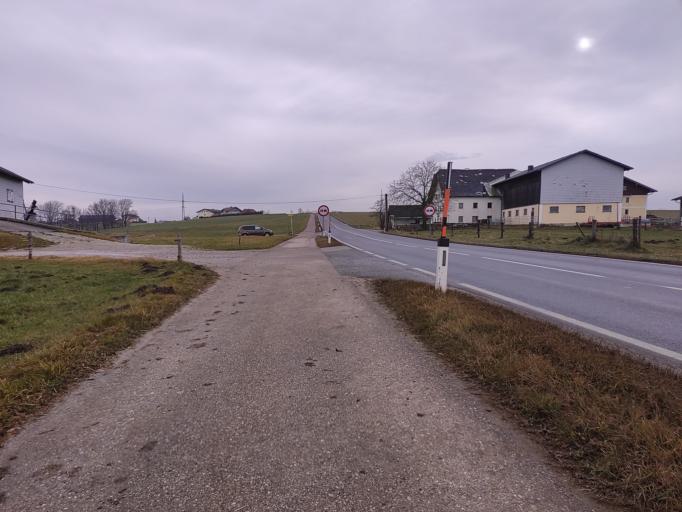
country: AT
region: Salzburg
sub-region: Politischer Bezirk Salzburg-Umgebung
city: Obertrum am See
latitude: 47.9257
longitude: 13.0936
